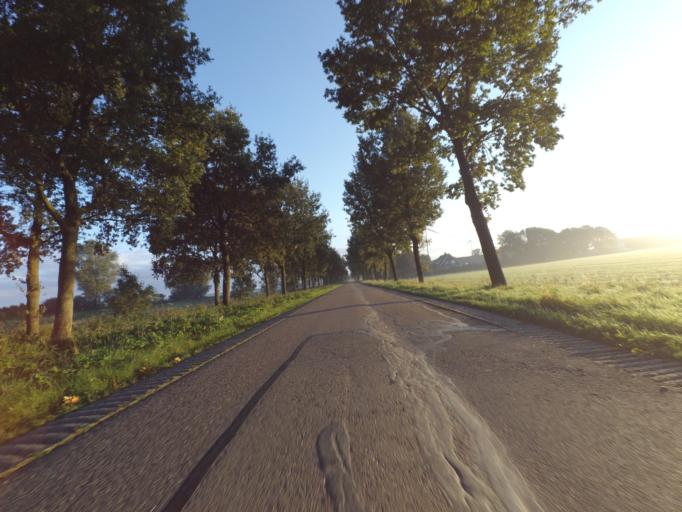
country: NL
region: Flevoland
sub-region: Gemeente Zeewolde
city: Zeewolde
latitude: 52.3787
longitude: 5.5292
